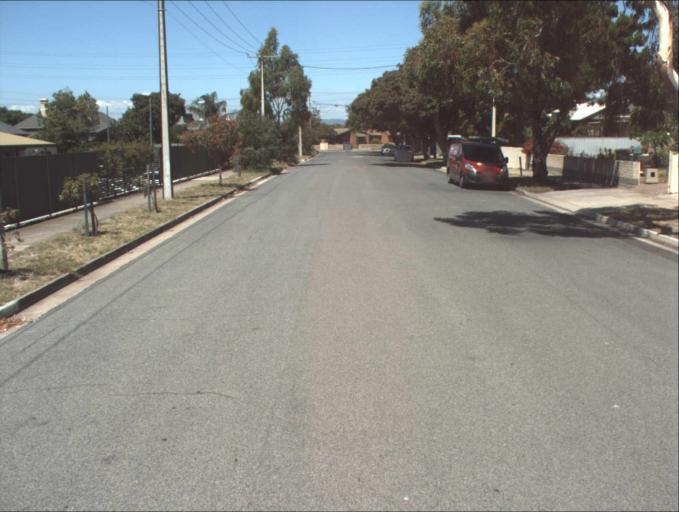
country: AU
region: South Australia
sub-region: Port Adelaide Enfield
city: Birkenhead
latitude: -34.8251
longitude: 138.4886
